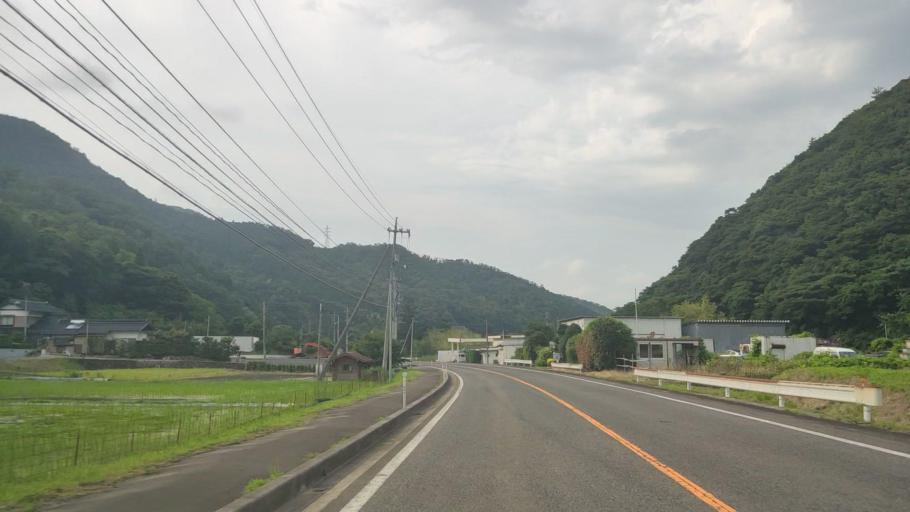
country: JP
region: Tottori
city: Kurayoshi
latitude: 35.3723
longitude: 133.8501
